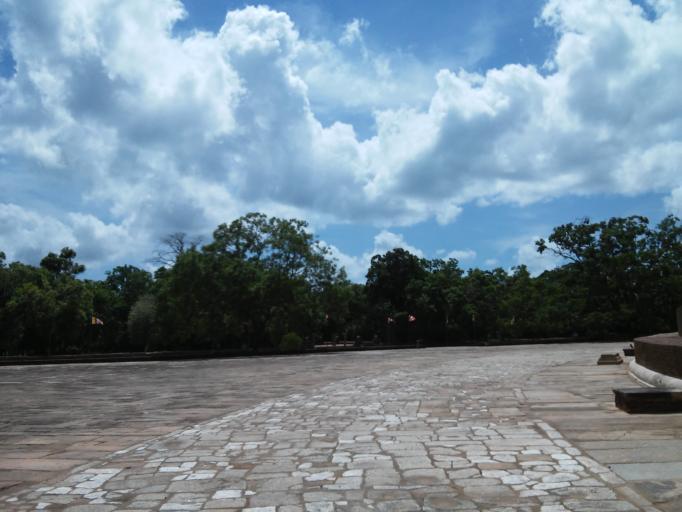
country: LK
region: North Central
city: Anuradhapura
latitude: 8.3705
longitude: 80.3950
